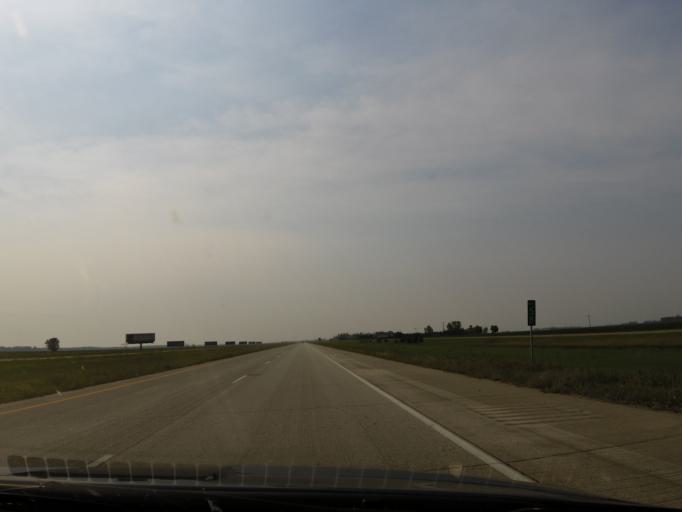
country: US
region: North Dakota
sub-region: Cass County
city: Horace
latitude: 46.7715
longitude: -96.8396
